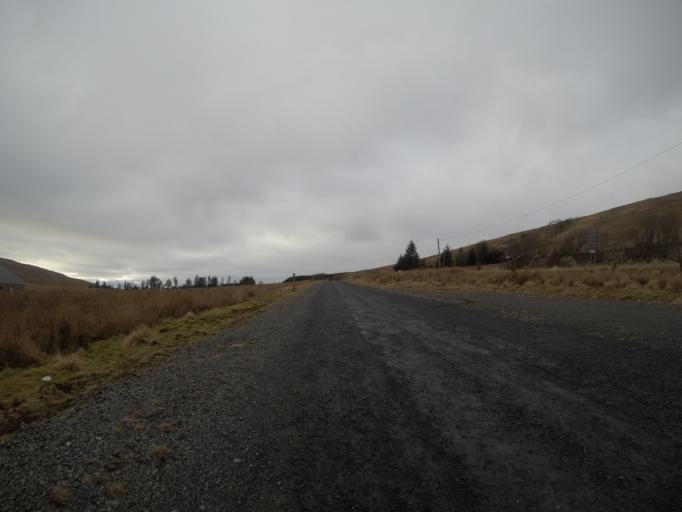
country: GB
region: Scotland
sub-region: North Ayrshire
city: Fairlie
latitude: 55.7788
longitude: -4.8045
